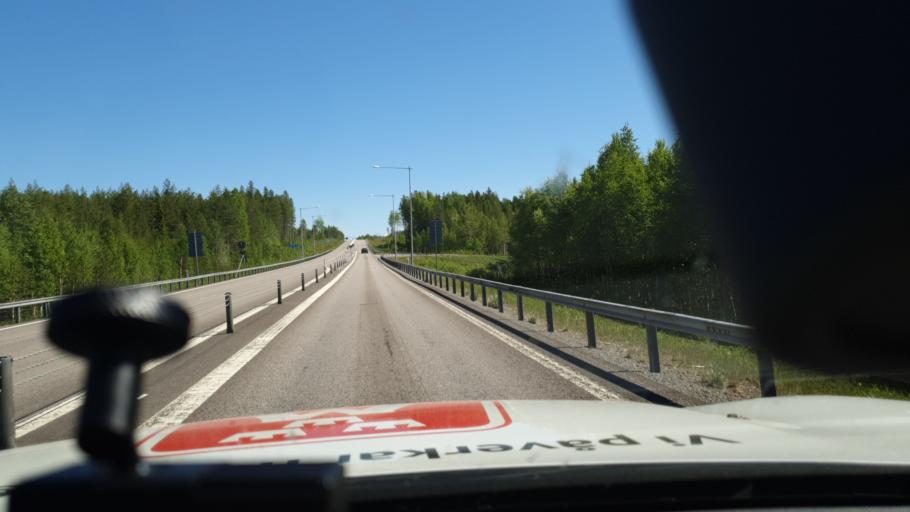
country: SE
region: Norrbotten
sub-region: Kalix Kommun
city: Toere
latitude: 65.9122
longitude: 22.8035
